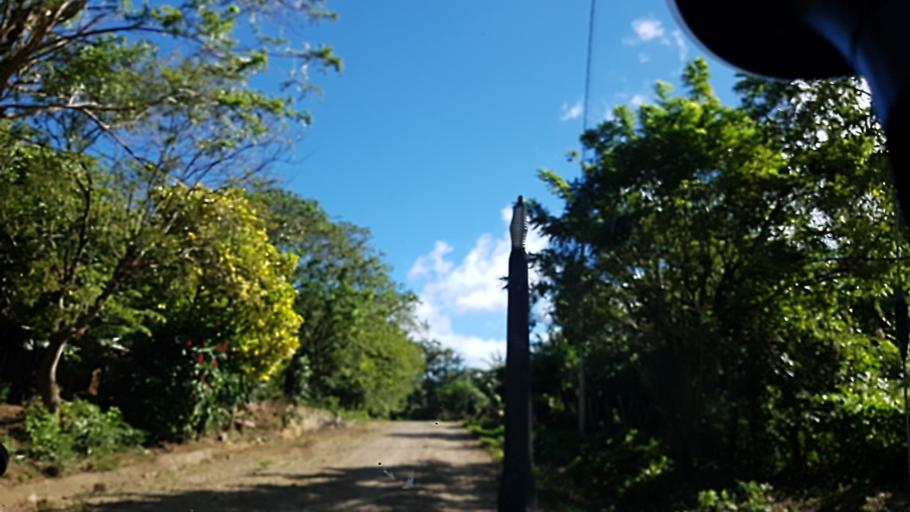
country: NI
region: Carazo
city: Santa Teresa
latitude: 11.6393
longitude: -86.1760
